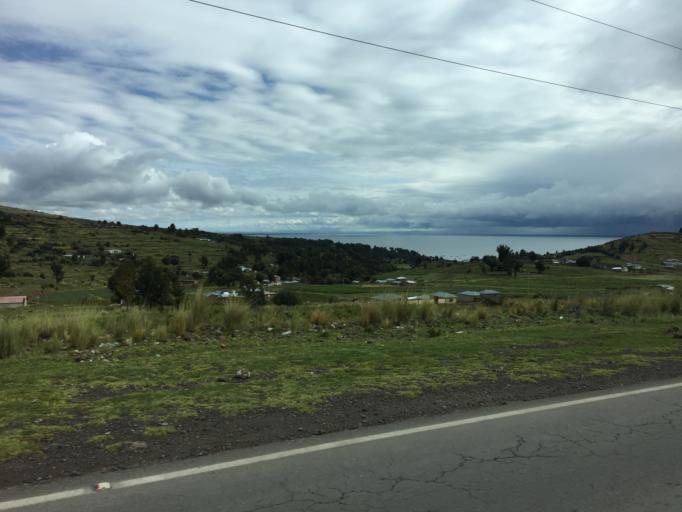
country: PE
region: Puno
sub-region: Provincia de Chucuito
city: Juli
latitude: -16.2022
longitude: -69.4206
